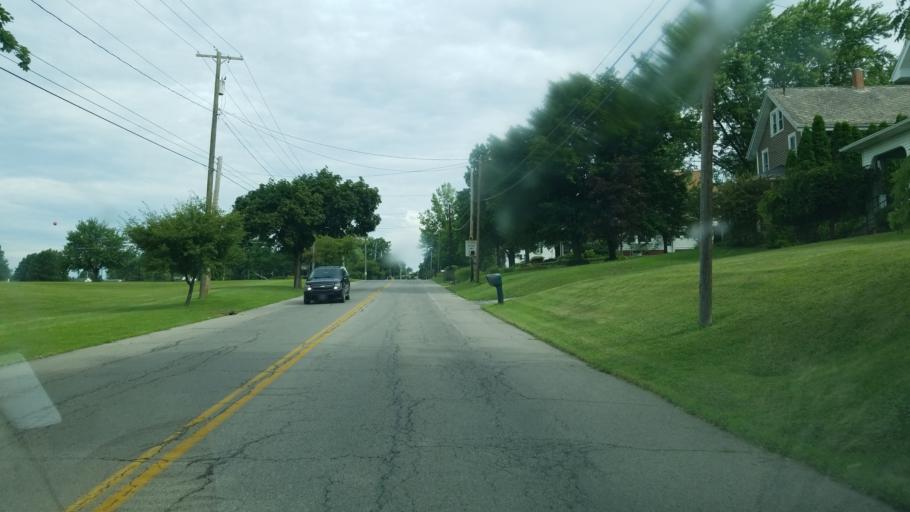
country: US
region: Ohio
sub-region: Ashland County
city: Ashland
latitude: 40.8558
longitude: -82.3087
